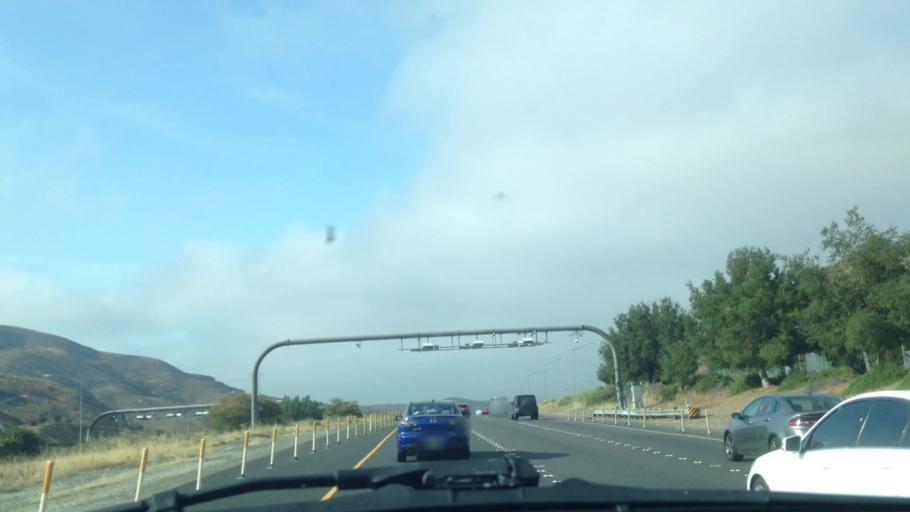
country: US
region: California
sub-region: Orange County
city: Villa Park
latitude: 33.8256
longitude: -117.7167
